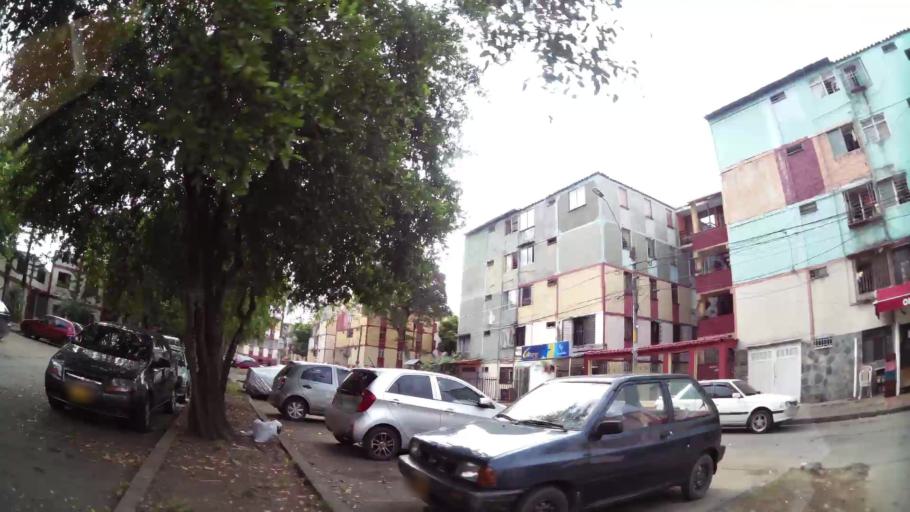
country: CO
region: Valle del Cauca
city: Cali
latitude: 3.4771
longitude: -76.4908
